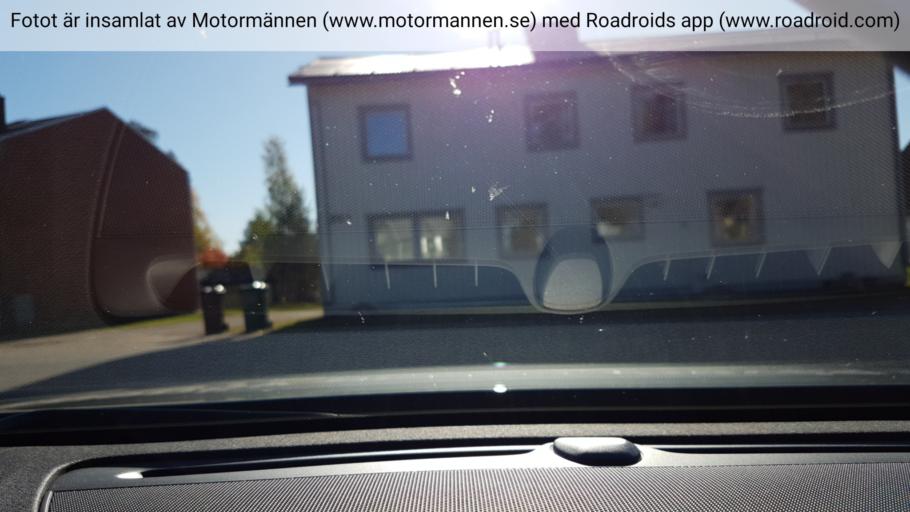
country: SE
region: Norrbotten
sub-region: Gallivare Kommun
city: Gaellivare
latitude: 66.4309
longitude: 20.6030
